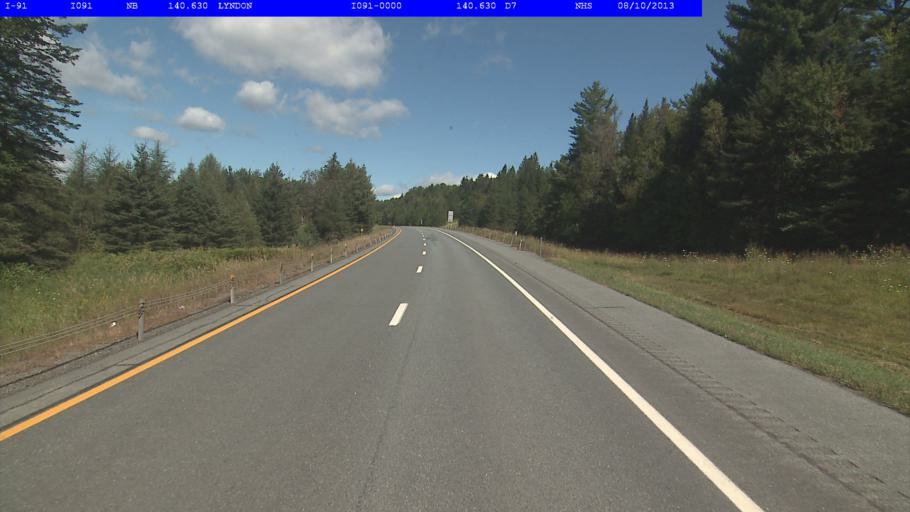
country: US
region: Vermont
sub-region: Caledonia County
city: Lyndonville
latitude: 44.5636
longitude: -72.0295
